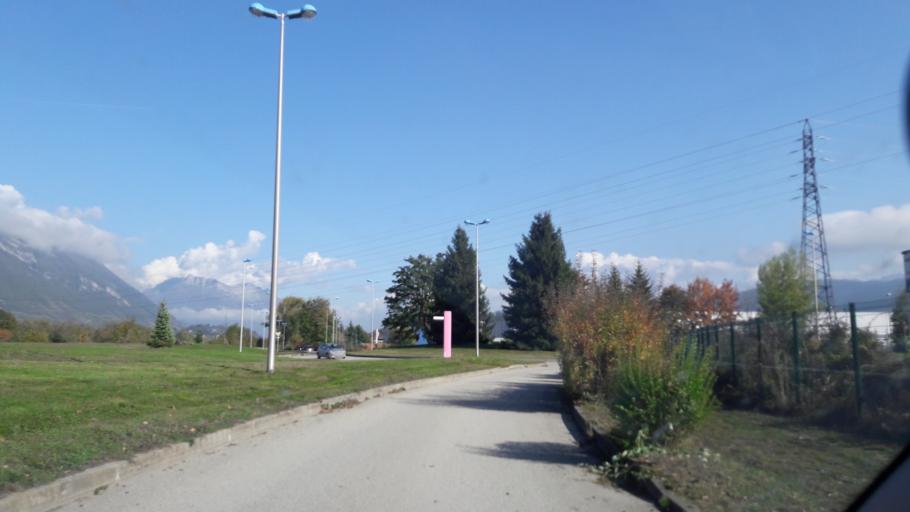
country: FR
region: Rhone-Alpes
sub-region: Departement de la Savoie
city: Les Marches
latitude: 45.4759
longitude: 6.0243
